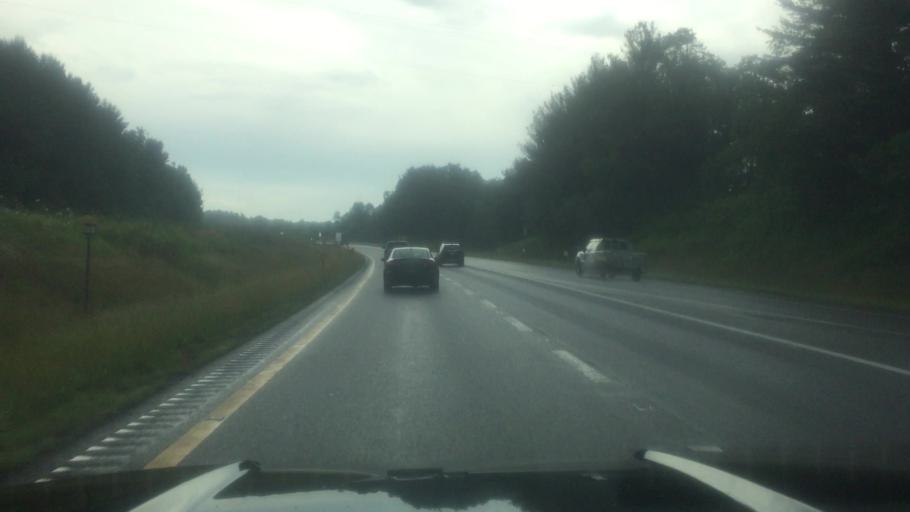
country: US
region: Virginia
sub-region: Carroll County
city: Hillsville
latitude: 36.6768
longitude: -80.7110
